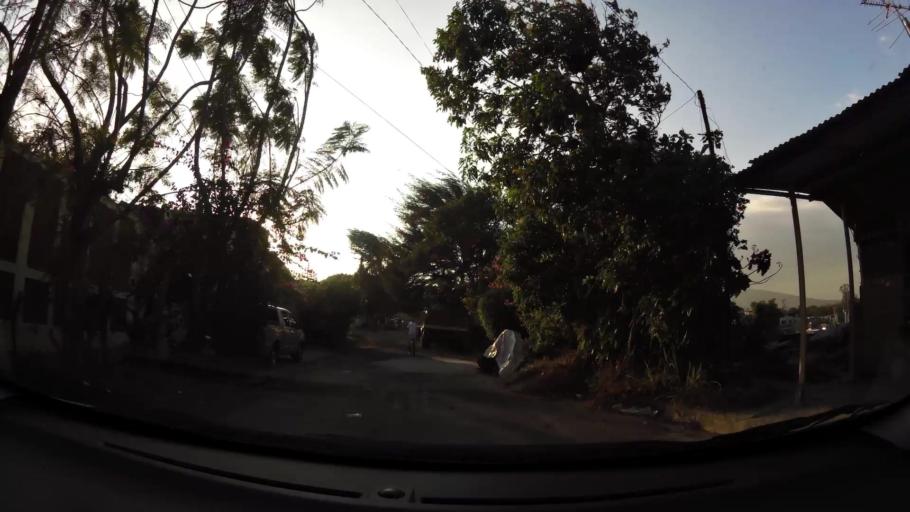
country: SV
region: San Salvador
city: Cuscatancingo
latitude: 13.7198
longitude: -89.1975
